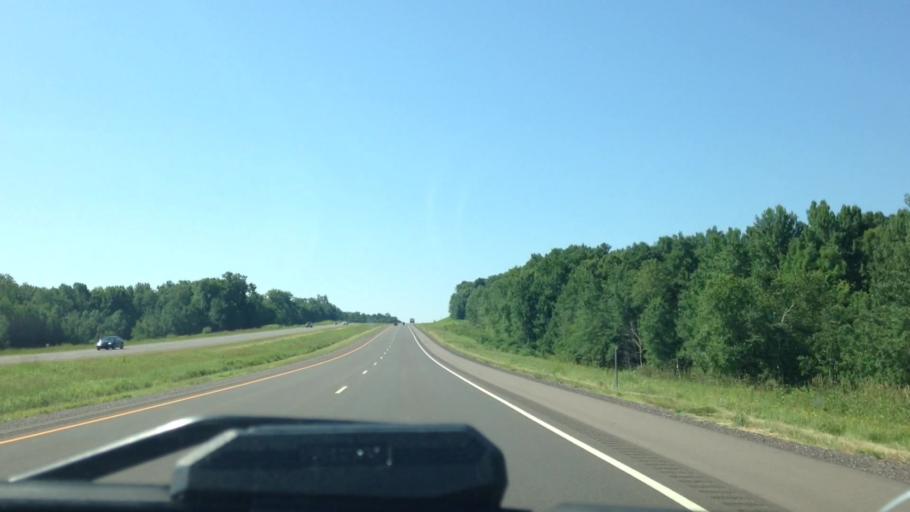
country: US
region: Wisconsin
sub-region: Washburn County
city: Spooner
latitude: 45.9777
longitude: -91.8277
